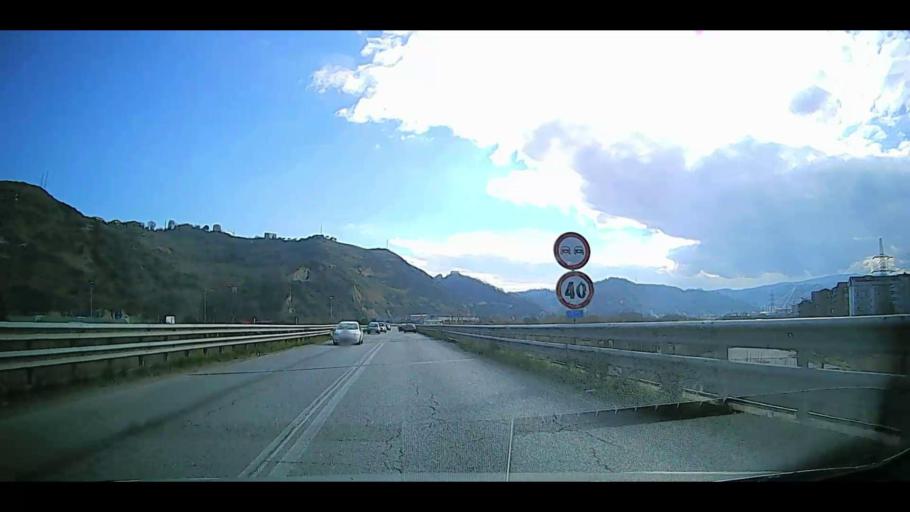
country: IT
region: Calabria
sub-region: Provincia di Cosenza
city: Cosenza
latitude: 39.3127
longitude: 16.2603
